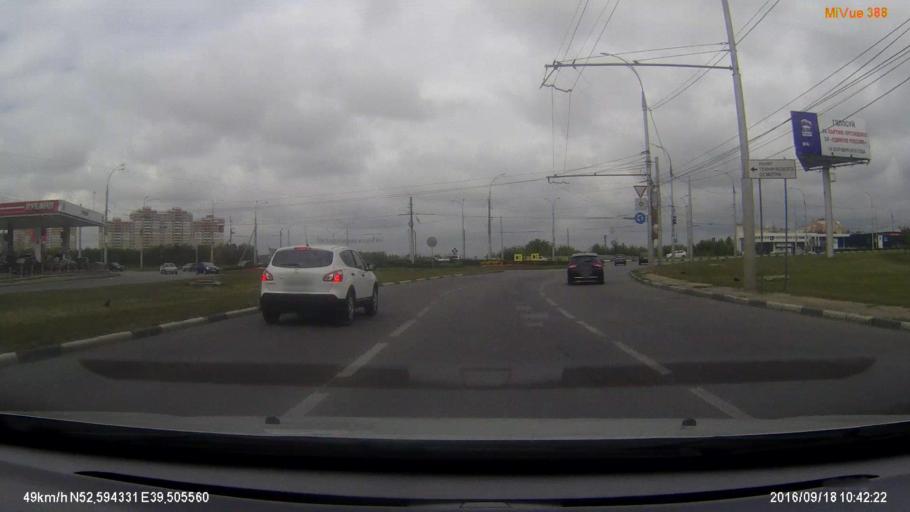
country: RU
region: Lipetsk
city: Syrskoye
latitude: 52.5942
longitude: 39.5059
